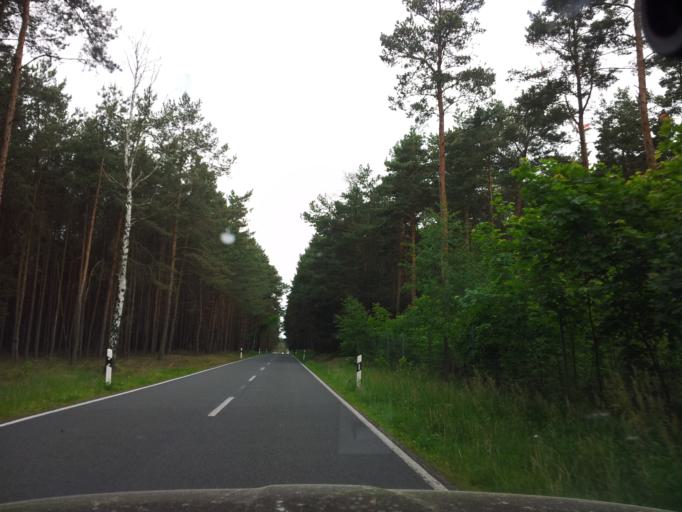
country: DE
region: Brandenburg
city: Linthe
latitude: 52.0833
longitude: 12.8015
